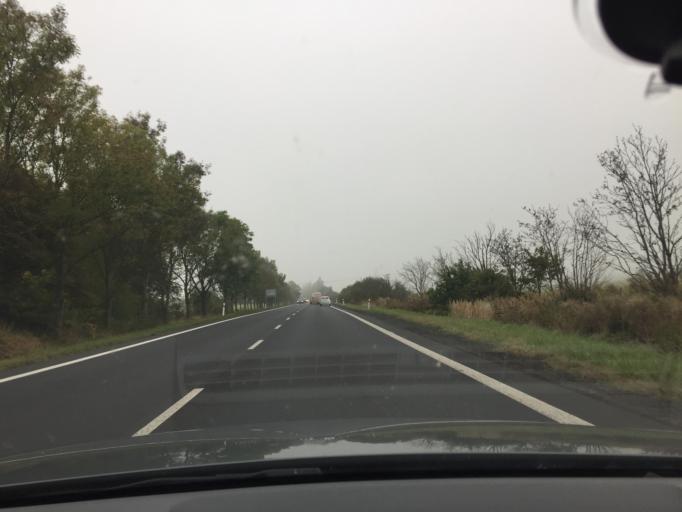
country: CZ
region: Ustecky
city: Libouchec
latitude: 50.7468
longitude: 14.0260
